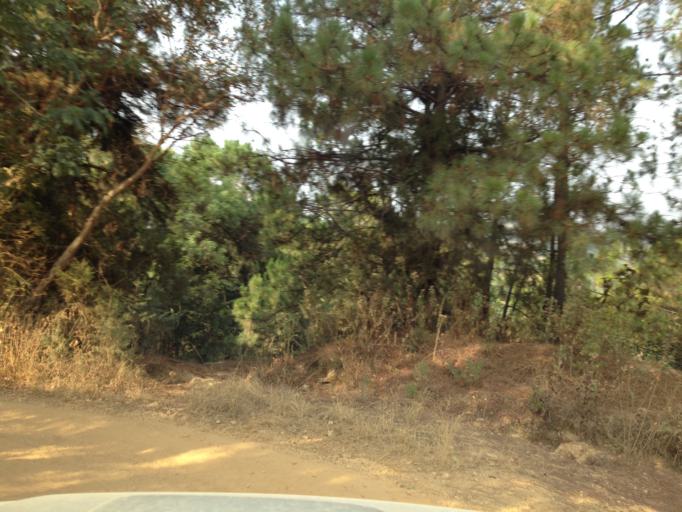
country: MX
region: Michoacan
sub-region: Zitacuaro
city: Macutzio
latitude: 19.4967
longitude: -100.3218
